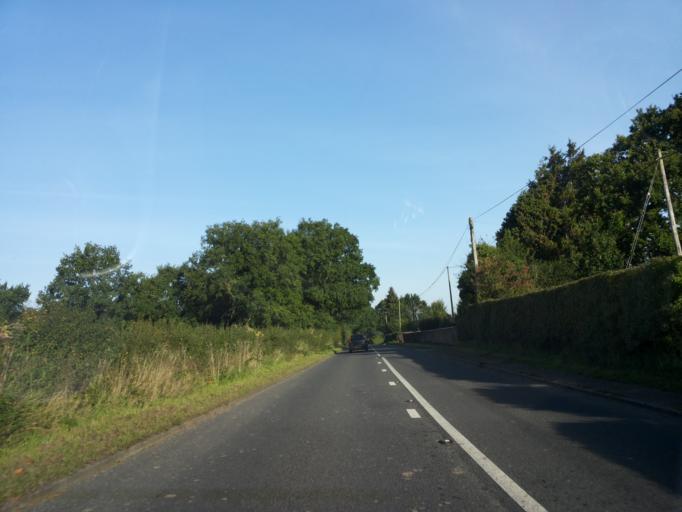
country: GB
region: England
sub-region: Warwickshire
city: Wroxall
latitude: 52.3407
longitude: -1.6816
